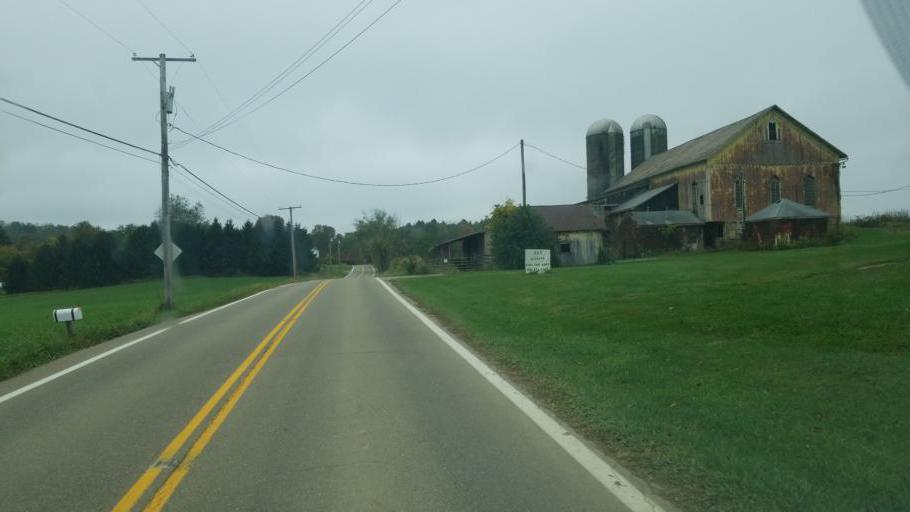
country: US
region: Ohio
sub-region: Tuscarawas County
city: Strasburg
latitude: 40.6565
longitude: -81.5030
